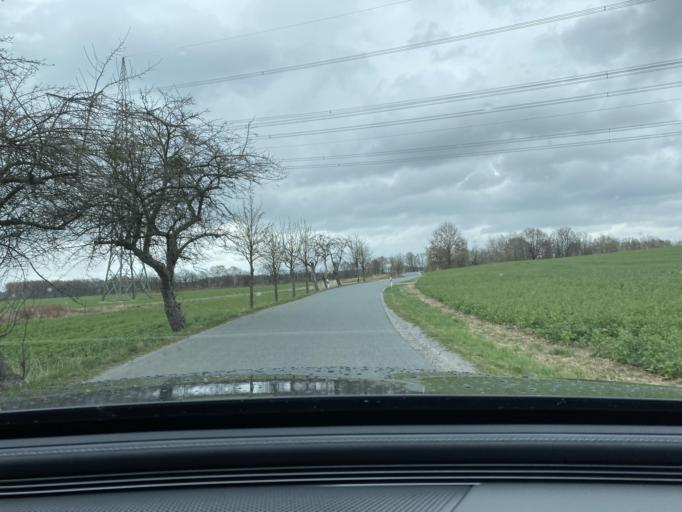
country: DE
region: Saxony
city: Radibor
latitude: 51.2486
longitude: 14.3735
